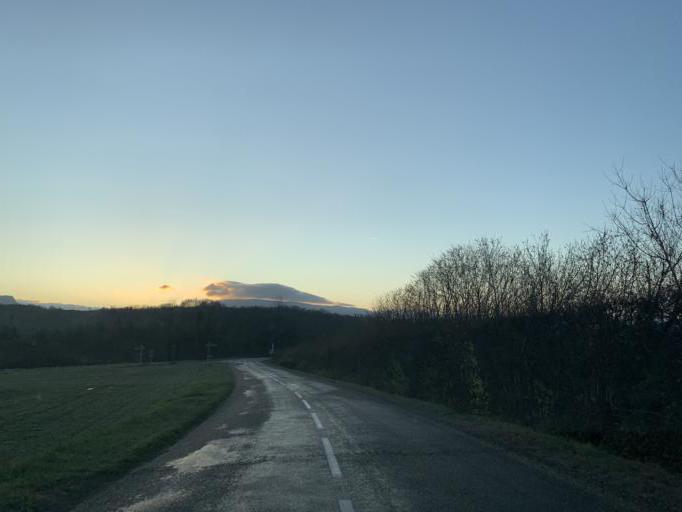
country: FR
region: Rhone-Alpes
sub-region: Departement de l'Ain
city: Belley
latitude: 45.7804
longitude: 5.6575
